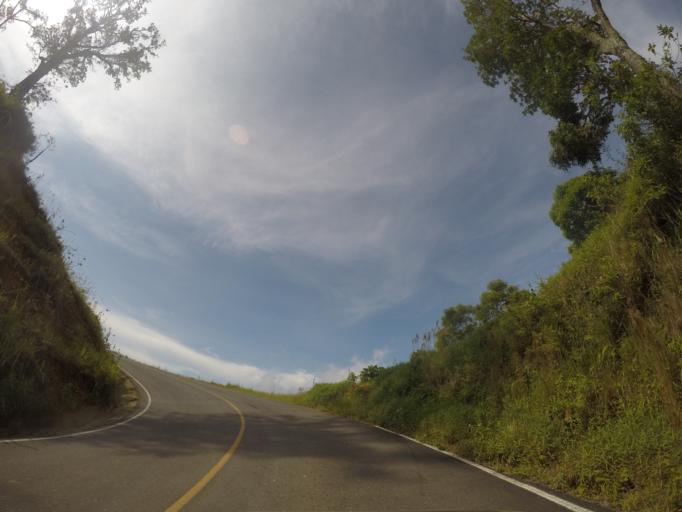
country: MX
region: Oaxaca
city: Pluma Hidalgo
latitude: 15.9308
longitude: -96.4240
